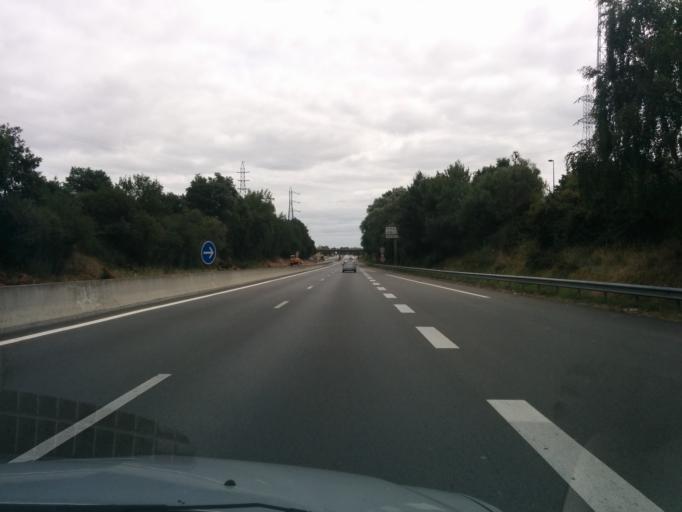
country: FR
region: Pays de la Loire
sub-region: Departement de la Loire-Atlantique
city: Sainte-Luce-sur-Loire
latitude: 47.2516
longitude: -1.5119
